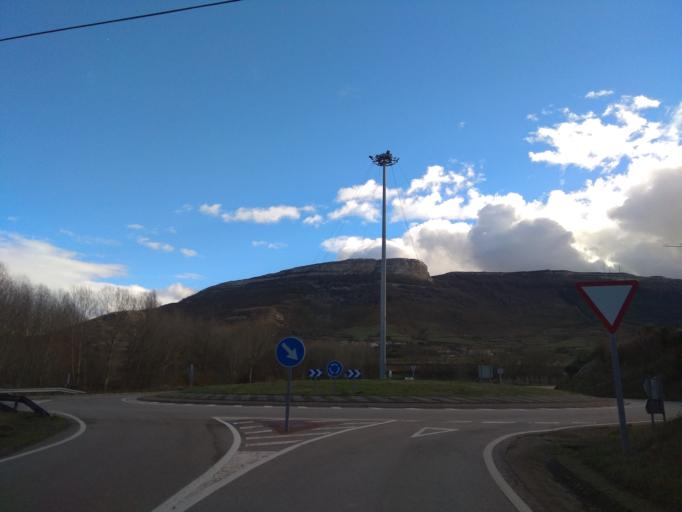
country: ES
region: Cantabria
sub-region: Provincia de Cantabria
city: San Martin de Elines
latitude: 42.8303
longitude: -3.9040
